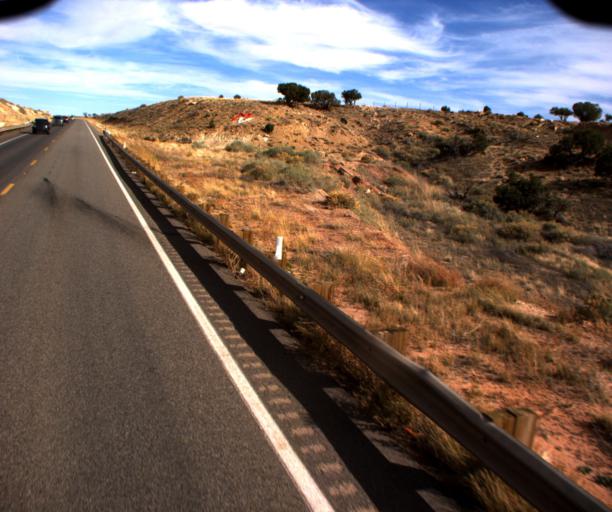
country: US
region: Arizona
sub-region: Navajo County
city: Kayenta
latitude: 36.6993
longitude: -110.3058
